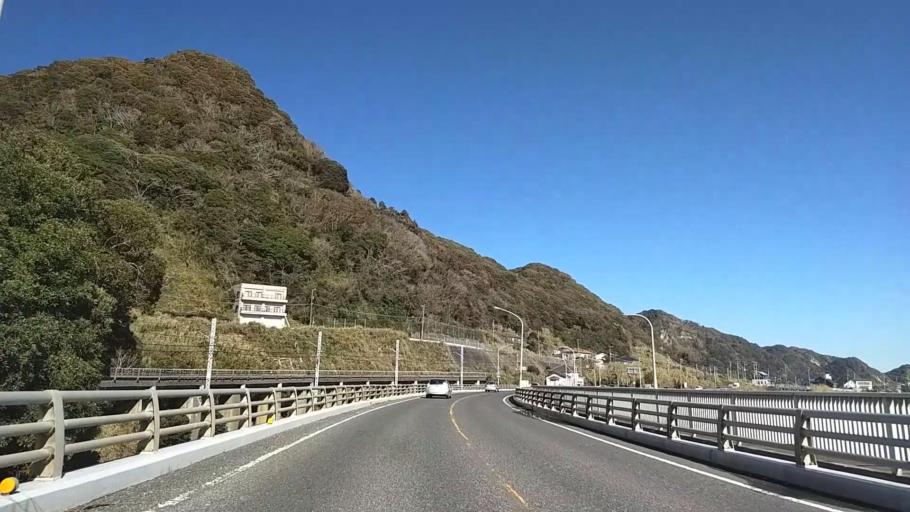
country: JP
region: Chiba
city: Kawaguchi
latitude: 35.0672
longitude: 140.0783
